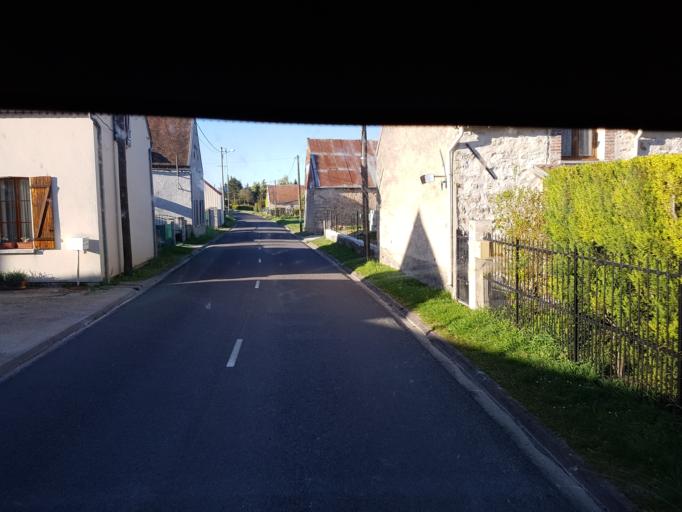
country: FR
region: Champagne-Ardenne
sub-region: Departement de l'Aube
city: Marigny-le-Chatel
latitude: 48.3972
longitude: 3.6568
